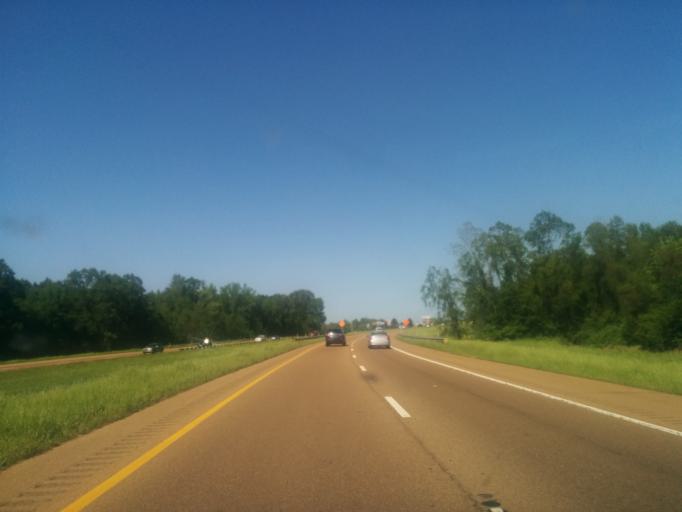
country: US
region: Mississippi
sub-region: Madison County
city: Madison
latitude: 32.5044
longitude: -90.1170
